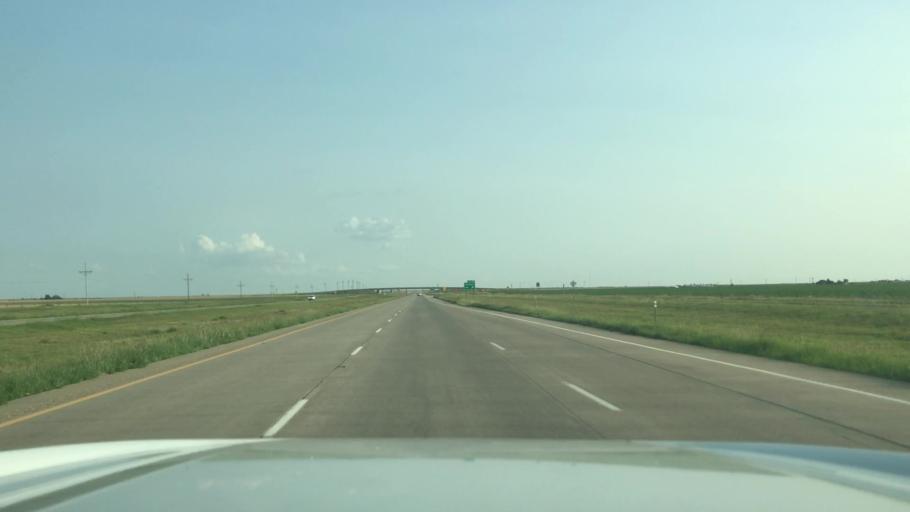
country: US
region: Texas
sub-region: Randall County
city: Canyon
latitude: 34.8477
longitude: -101.8489
